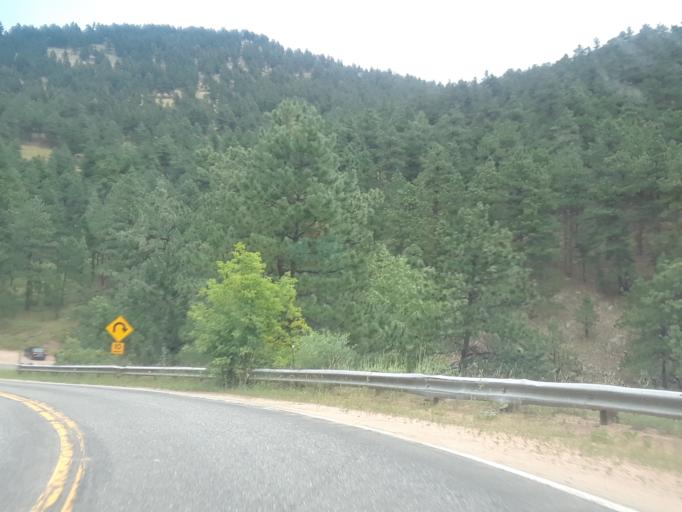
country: US
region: Colorado
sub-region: Boulder County
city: Boulder
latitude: 40.0326
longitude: -105.3163
